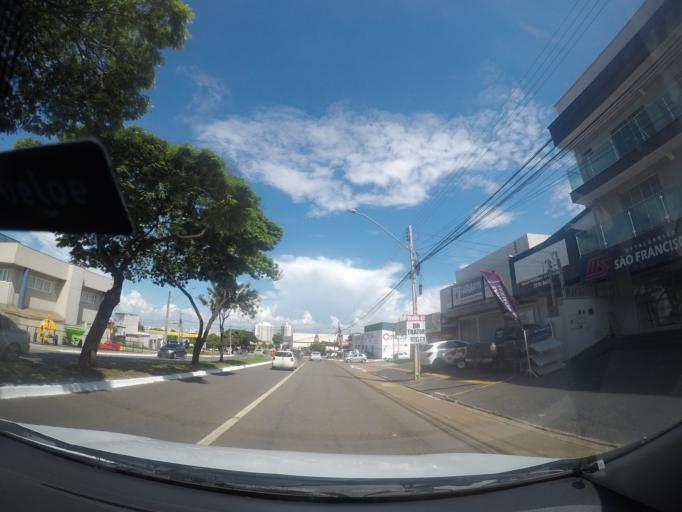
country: BR
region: Goias
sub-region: Goiania
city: Goiania
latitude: -16.6641
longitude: -49.3256
